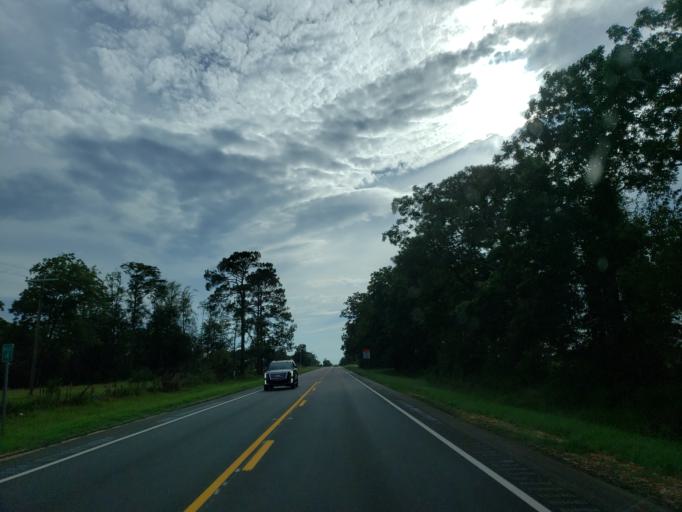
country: US
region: Georgia
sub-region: Irwin County
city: Ocilla
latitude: 31.5643
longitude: -83.3438
